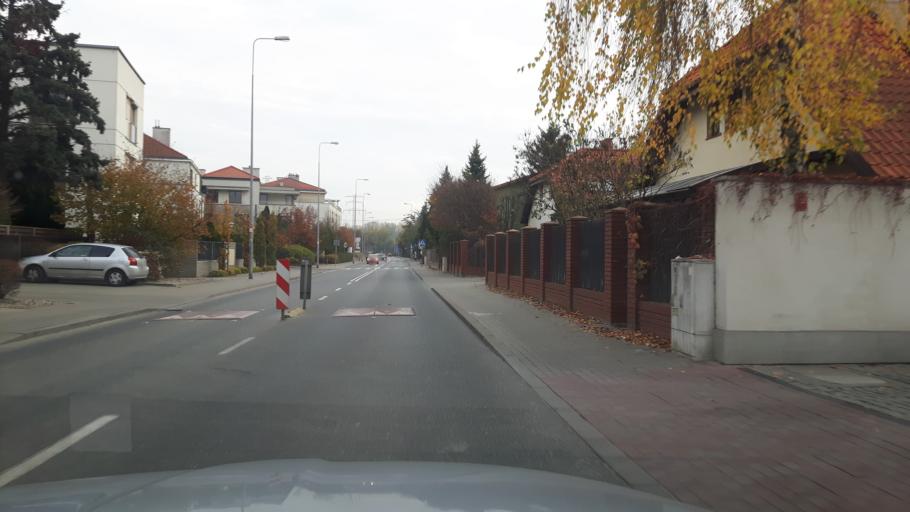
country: PL
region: Masovian Voivodeship
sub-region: Warszawa
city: Wilanow
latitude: 52.1681
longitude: 21.1075
